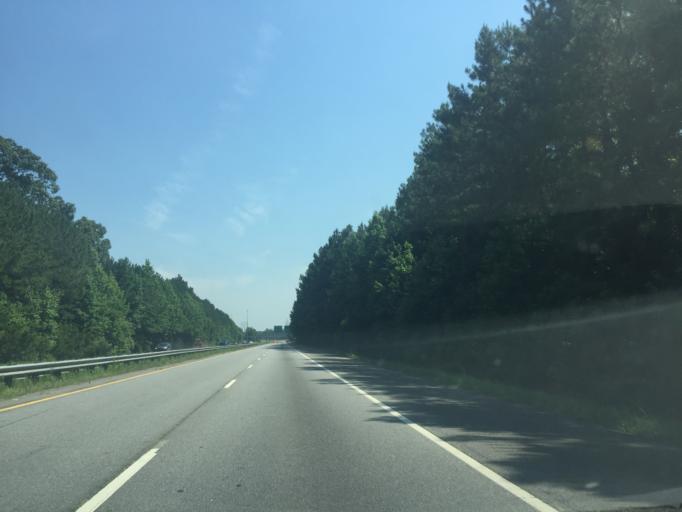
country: US
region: Georgia
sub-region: Chatham County
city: Georgetown
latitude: 32.0324
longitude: -81.1671
